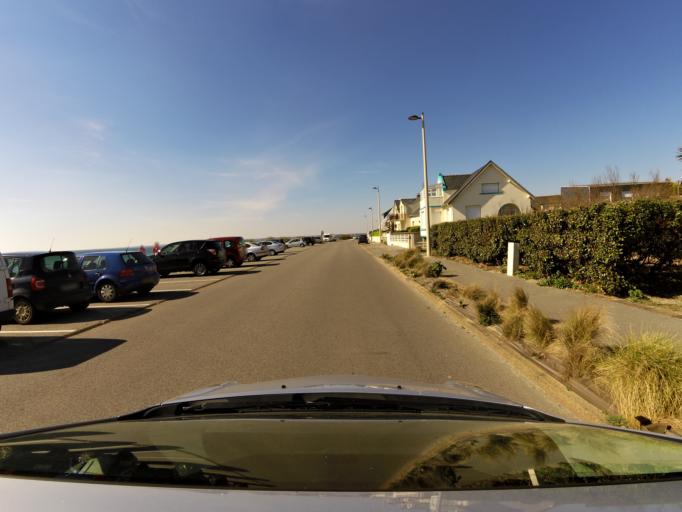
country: FR
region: Brittany
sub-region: Departement du Morbihan
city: Guidel-Plage
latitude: 47.7350
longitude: -3.4999
